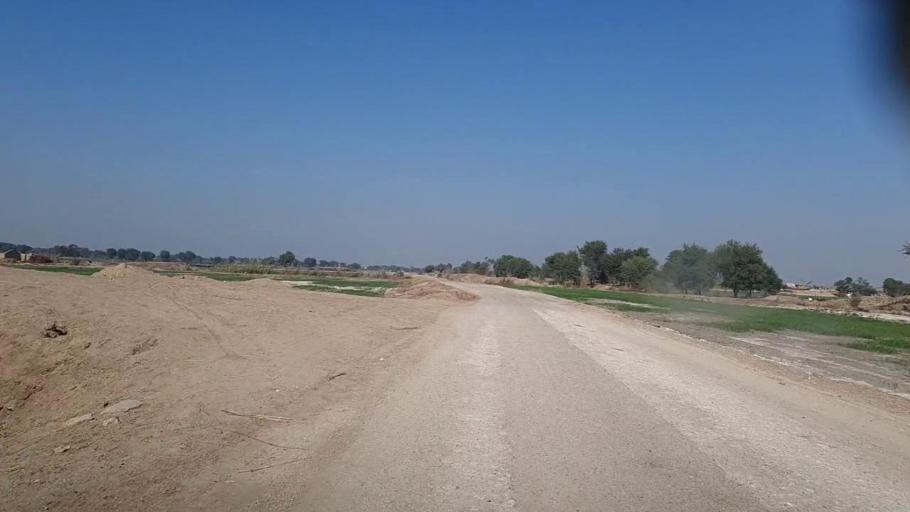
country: PK
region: Sindh
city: Khairpur
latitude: 27.9847
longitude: 69.8491
